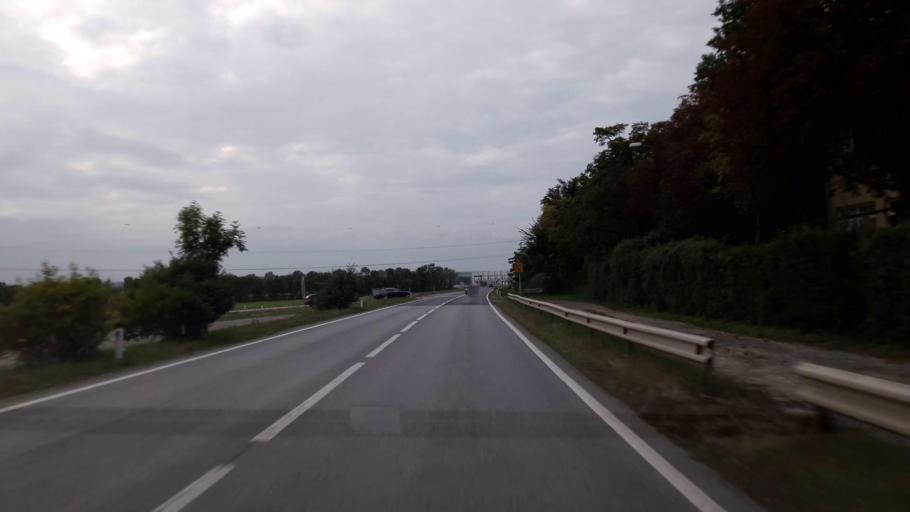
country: AT
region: Lower Austria
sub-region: Politischer Bezirk Bruck an der Leitha
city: Enzersdorf an der Fischa
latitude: 48.0618
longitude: 16.6188
